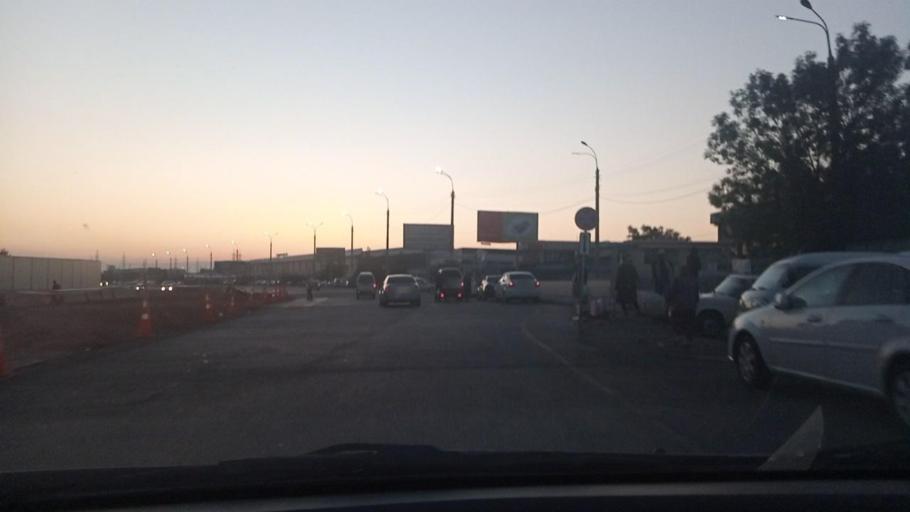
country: UZ
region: Toshkent Shahri
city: Bektemir
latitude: 41.2384
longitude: 69.3322
